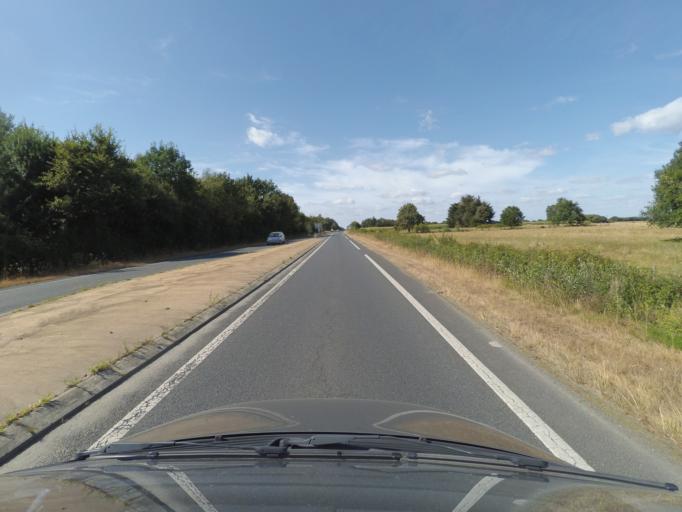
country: FR
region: Pays de la Loire
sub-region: Departement de la Loire-Atlantique
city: Le Bignon
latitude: 47.0916
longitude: -1.5299
